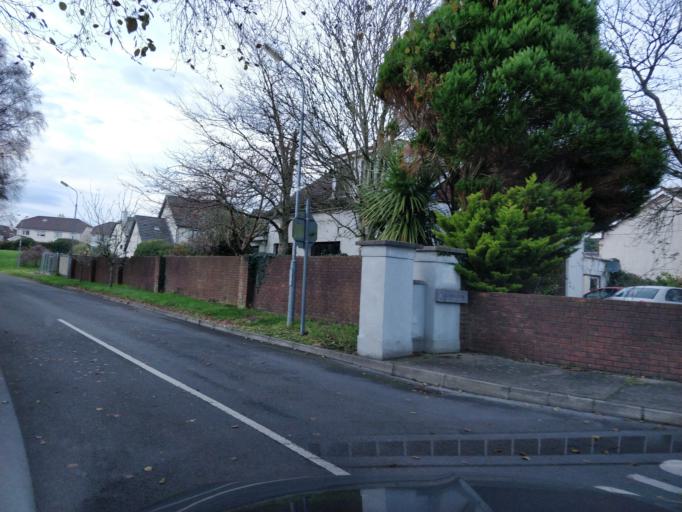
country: IE
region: Connaught
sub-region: County Galway
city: Bearna
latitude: 53.2654
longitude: -9.1062
